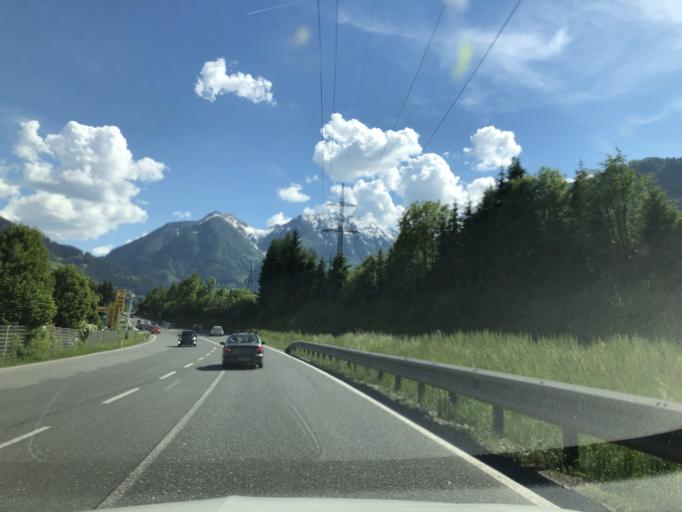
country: AT
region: Salzburg
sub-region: Politischer Bezirk Sankt Johann im Pongau
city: Sankt Johann im Pongau
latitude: 47.3480
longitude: 13.1868
